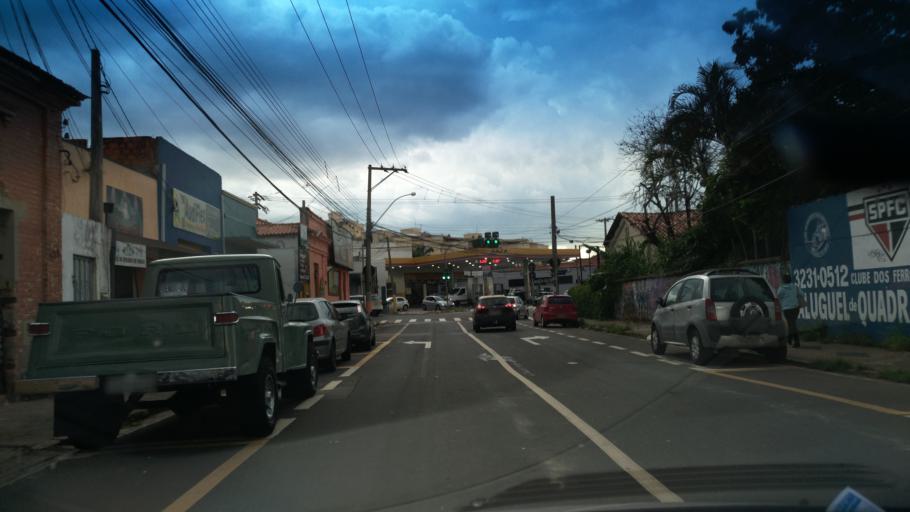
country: BR
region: Sao Paulo
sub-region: Campinas
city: Campinas
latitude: -22.9161
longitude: -47.0566
